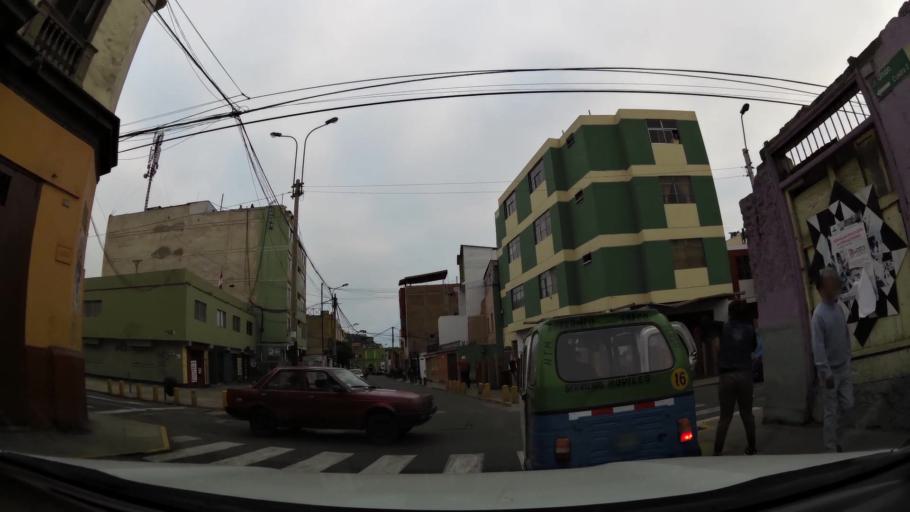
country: PE
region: Lima
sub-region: Lima
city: Surco
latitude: -12.1468
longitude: -77.0205
